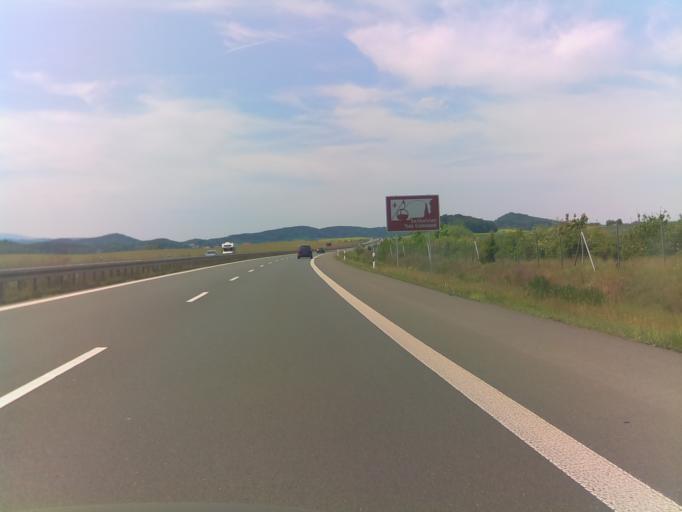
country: DE
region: Saxony-Anhalt
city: Westerhausen
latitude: 51.8121
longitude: 11.1041
